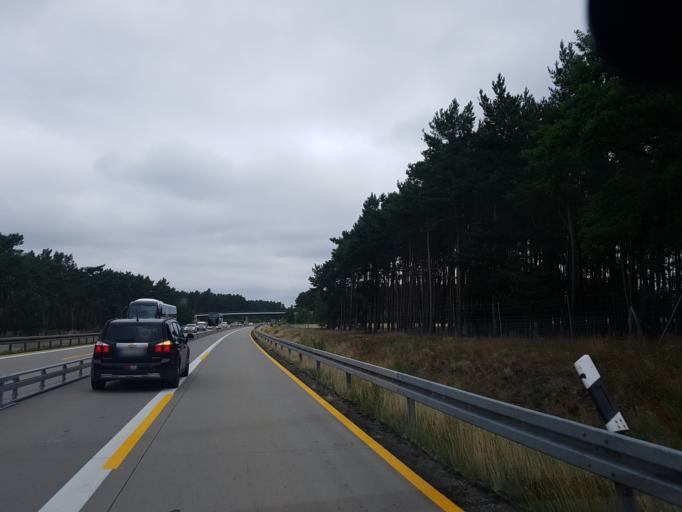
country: DE
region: Brandenburg
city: Kasel-Golzig
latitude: 51.9372
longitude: 13.7635
